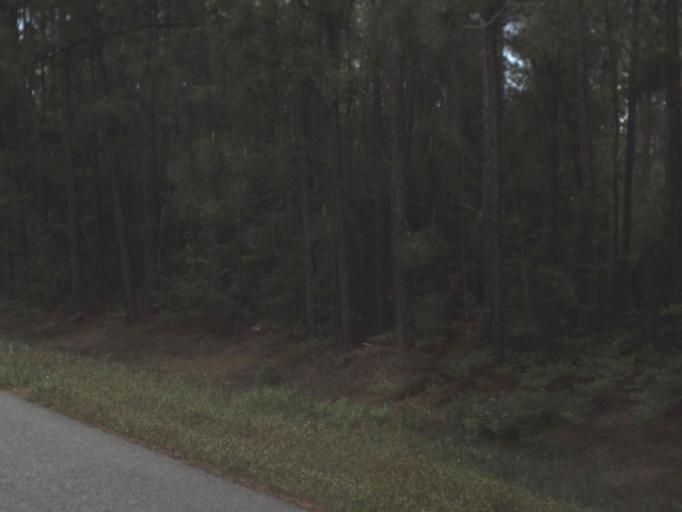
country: US
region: Florida
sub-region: Escambia County
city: Molino
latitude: 30.8141
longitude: -87.4285
